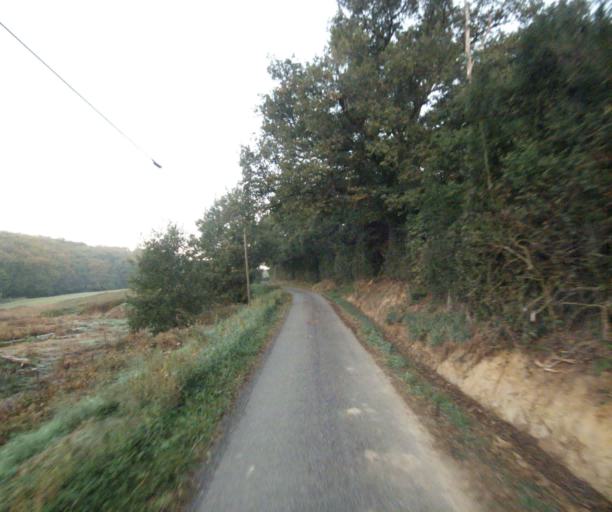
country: FR
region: Midi-Pyrenees
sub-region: Departement du Gers
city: Vic-Fezensac
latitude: 43.7764
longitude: 0.2301
